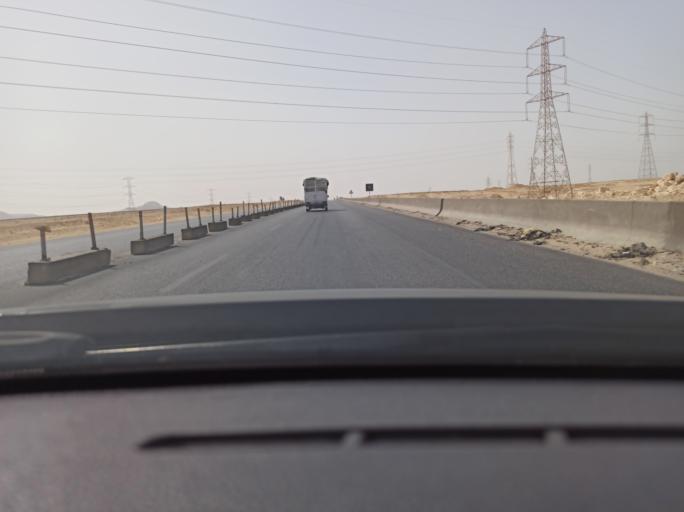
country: EG
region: Muhafazat Bani Suwayf
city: Bush
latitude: 29.1485
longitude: 31.2320
